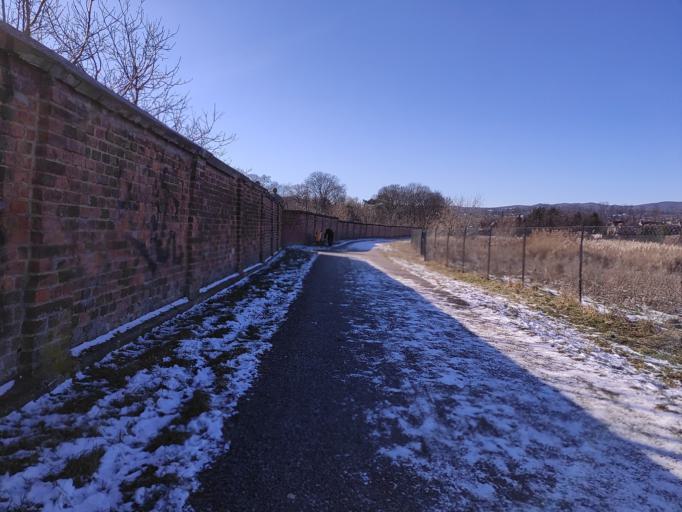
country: AT
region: Lower Austria
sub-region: Politischer Bezirk Modling
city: Modling
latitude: 48.0964
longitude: 16.2997
